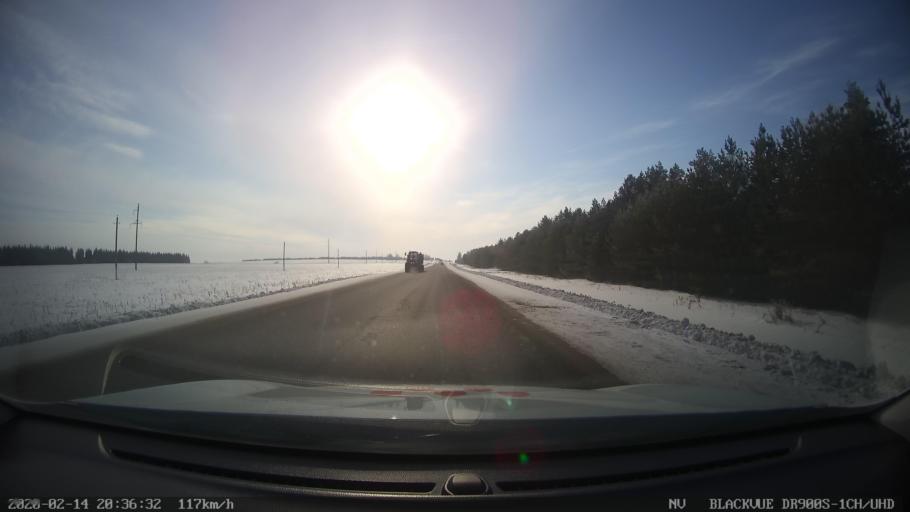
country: RU
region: Tatarstan
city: Kuybyshevskiy Zaton
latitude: 55.3658
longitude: 49.0005
